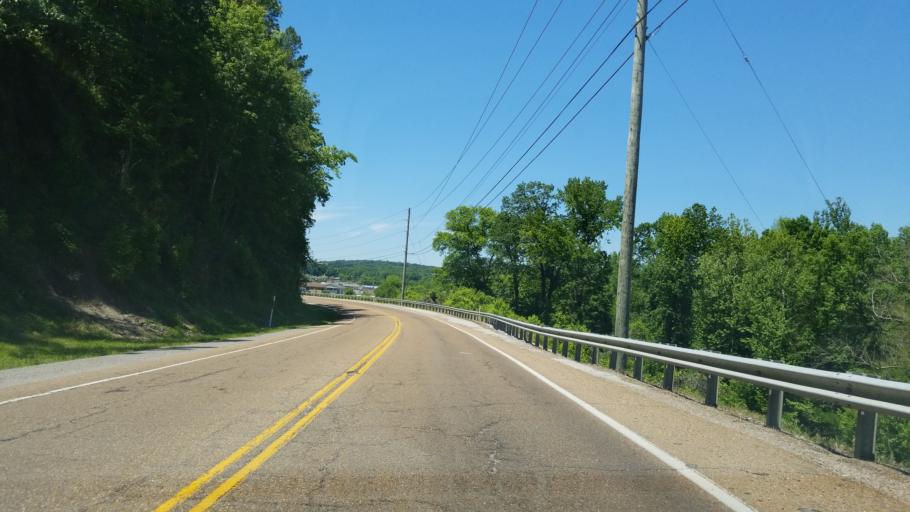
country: US
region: Tennessee
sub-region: Hamilton County
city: Collegedale
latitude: 35.0575
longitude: -85.0584
